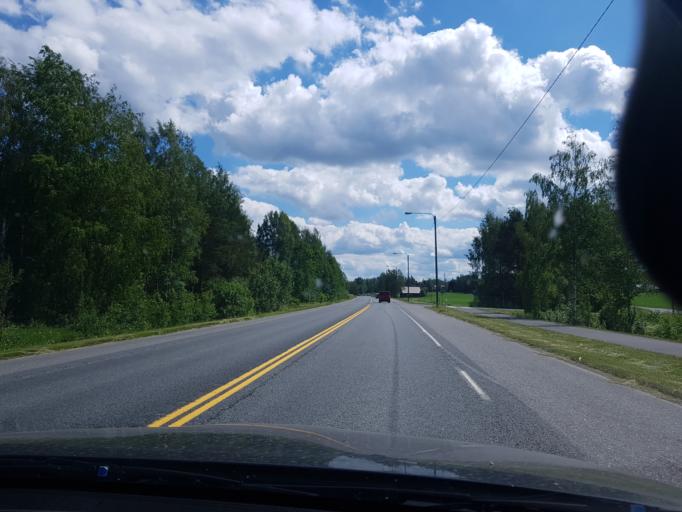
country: FI
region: Haeme
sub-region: Haemeenlinna
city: Parola
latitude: 61.0435
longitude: 24.3996
